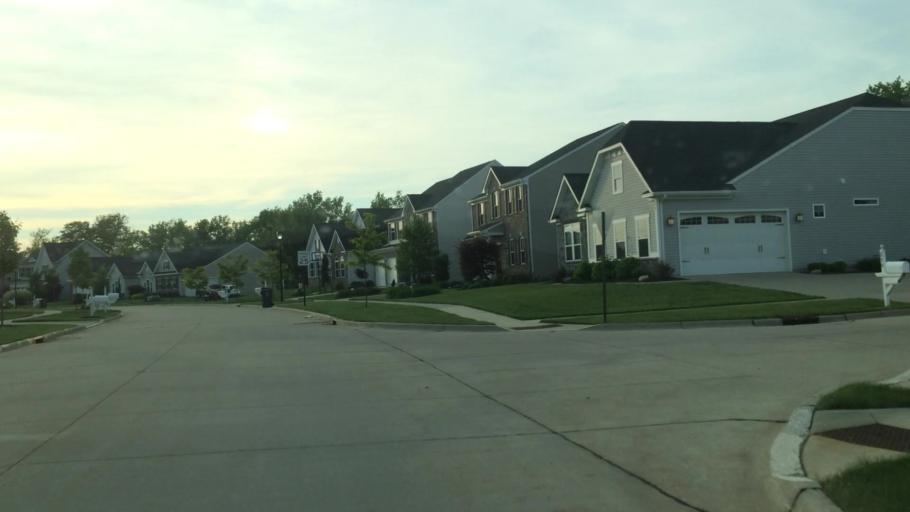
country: US
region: Ohio
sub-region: Medina County
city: Wadsworth
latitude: 41.0661
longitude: -81.7235
